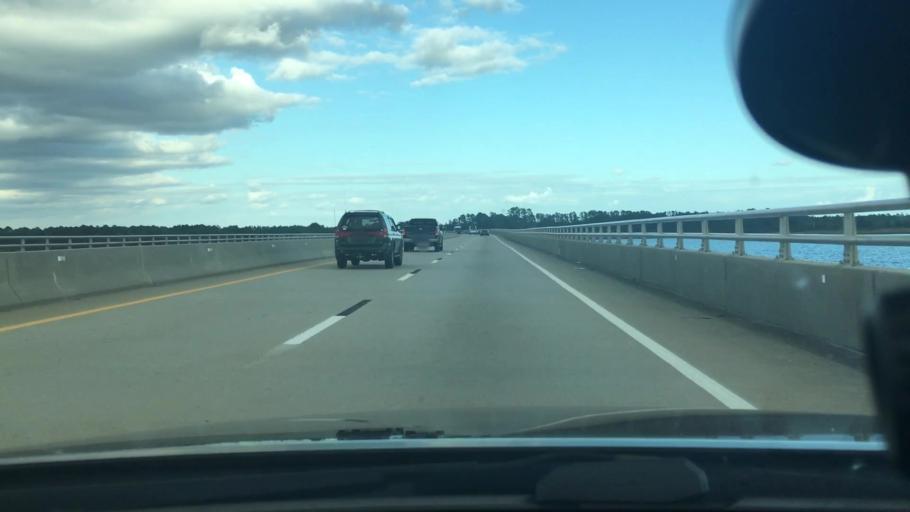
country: US
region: North Carolina
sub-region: Craven County
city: James City
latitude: 35.0990
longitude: -77.0174
